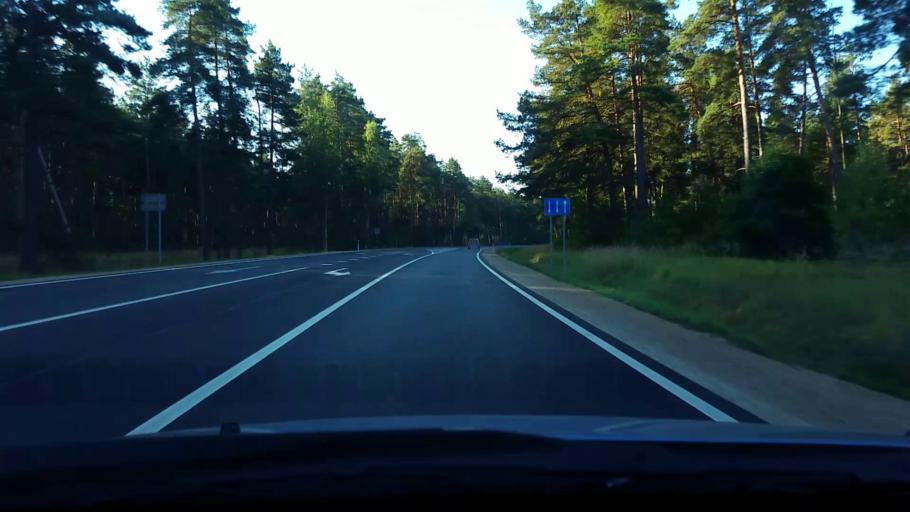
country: LV
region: Adazi
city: Adazi
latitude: 57.0297
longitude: 24.3208
